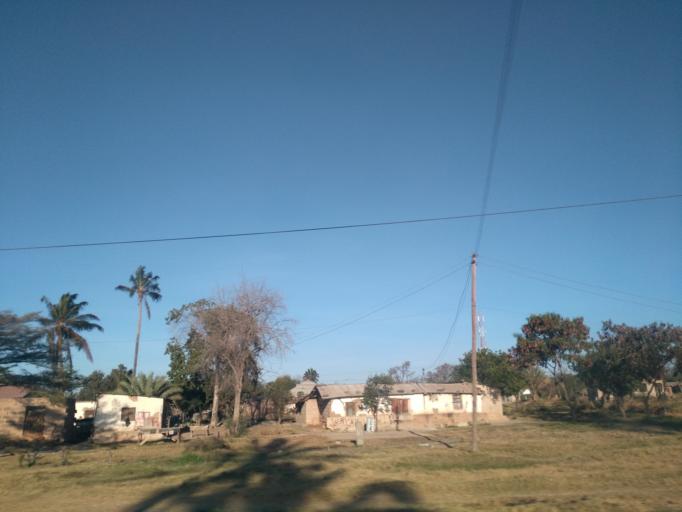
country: TZ
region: Dodoma
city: Dodoma
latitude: -6.1521
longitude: 35.7476
